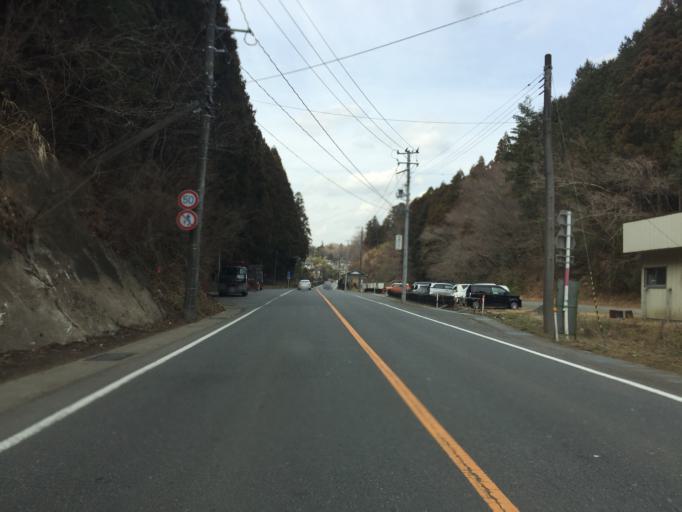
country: JP
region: Fukushima
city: Iwaki
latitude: 36.9727
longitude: 140.7399
